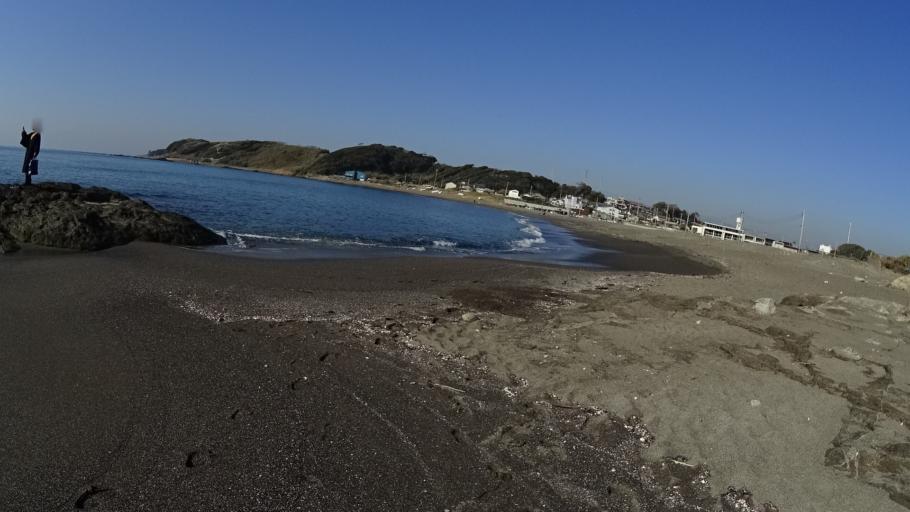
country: JP
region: Kanagawa
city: Miura
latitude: 35.1881
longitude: 139.6173
